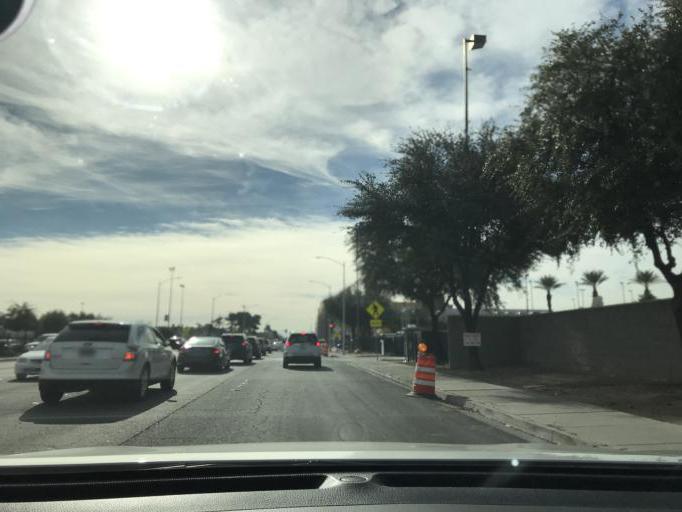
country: US
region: Nevada
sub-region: Clark County
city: Winchester
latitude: 36.1291
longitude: -115.1460
